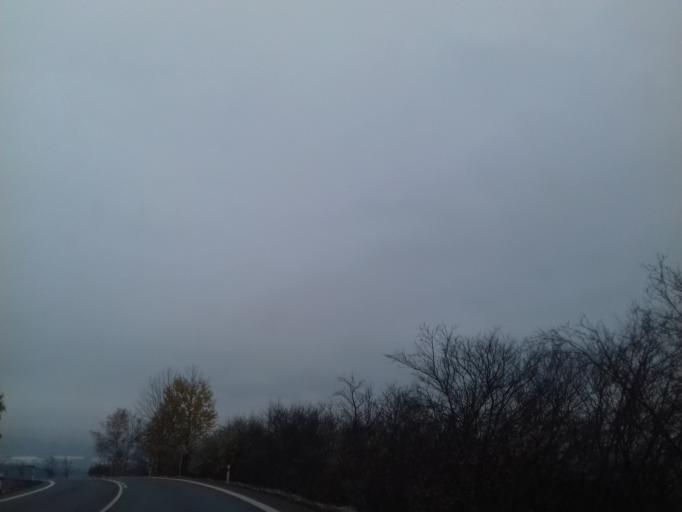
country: CZ
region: Plzensky
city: Meclov
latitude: 49.4569
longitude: 12.8673
